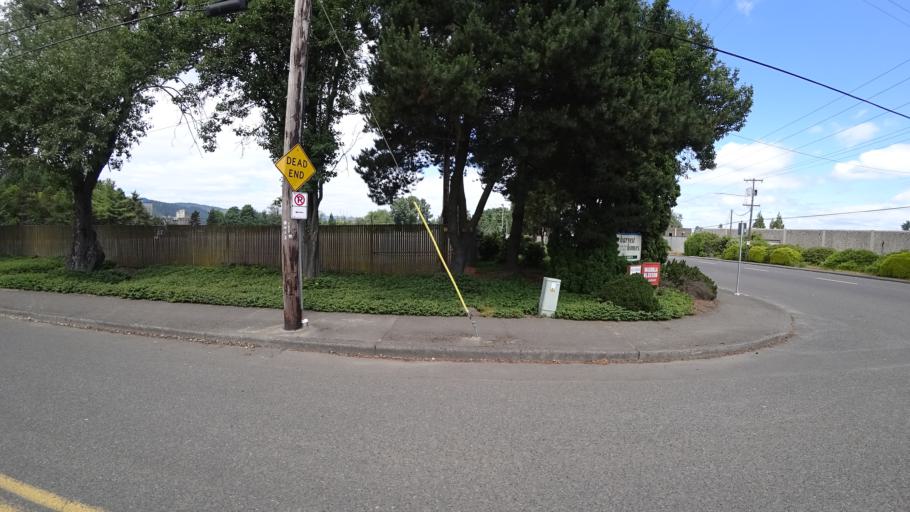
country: US
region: Oregon
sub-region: Washington County
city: West Haven
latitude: 45.6038
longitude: -122.7651
